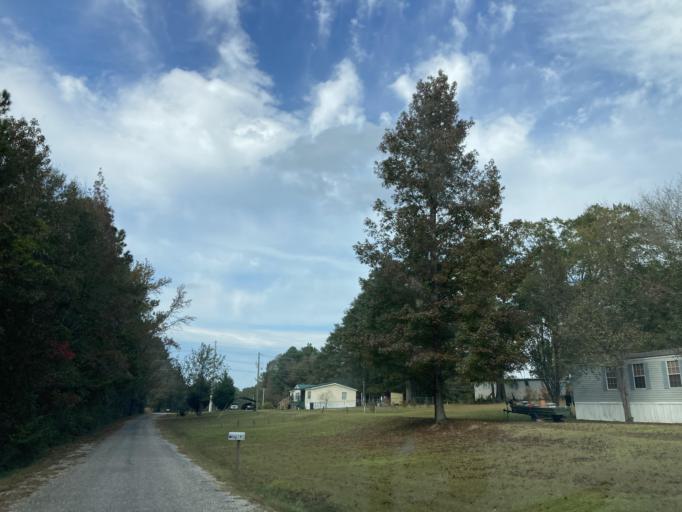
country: US
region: Mississippi
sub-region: Lamar County
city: West Hattiesburg
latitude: 31.3326
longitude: -89.4306
